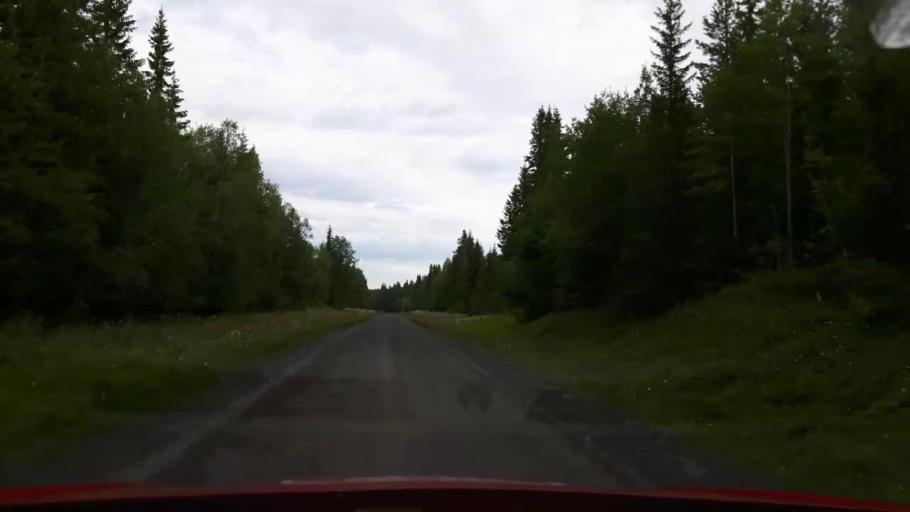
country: SE
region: Jaemtland
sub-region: OEstersunds Kommun
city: Lit
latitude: 63.4038
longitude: 15.2336
